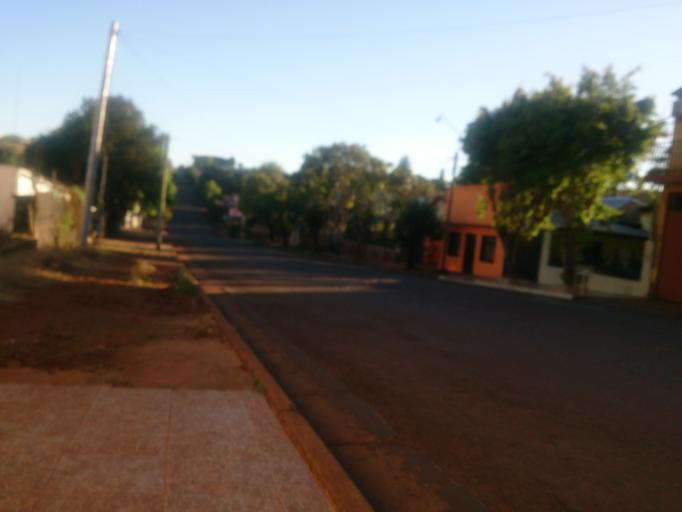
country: AR
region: Misiones
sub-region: Departamento de Obera
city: Obera
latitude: -27.4924
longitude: -55.1192
